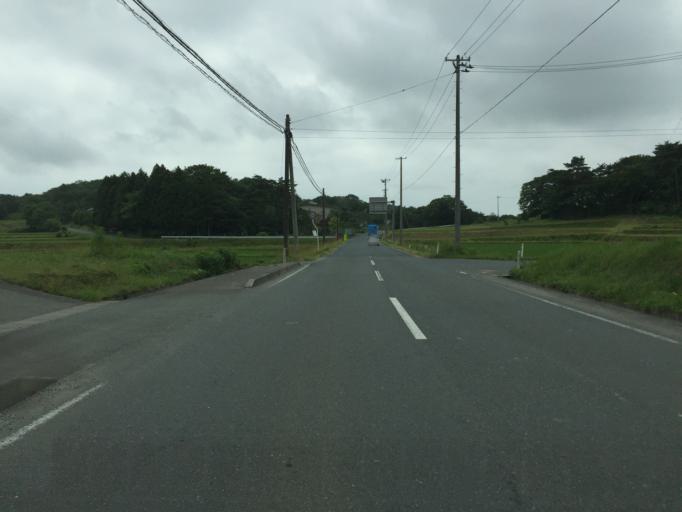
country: JP
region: Miyagi
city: Marumori
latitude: 37.7535
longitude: 140.9562
